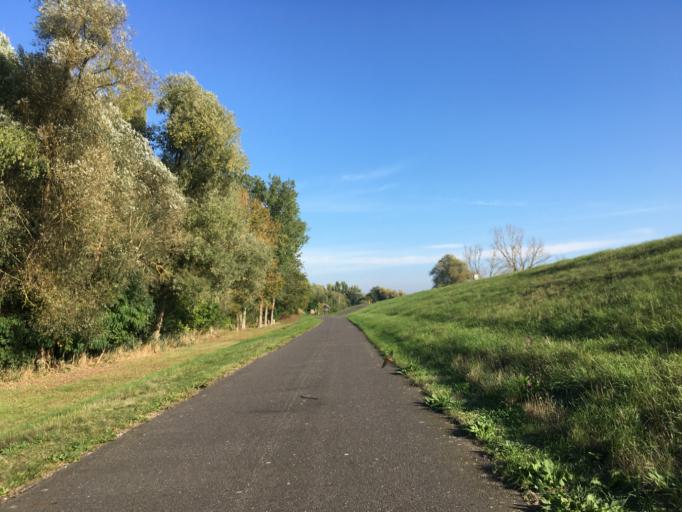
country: DE
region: Brandenburg
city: Reitwein
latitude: 52.5329
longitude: 14.6019
